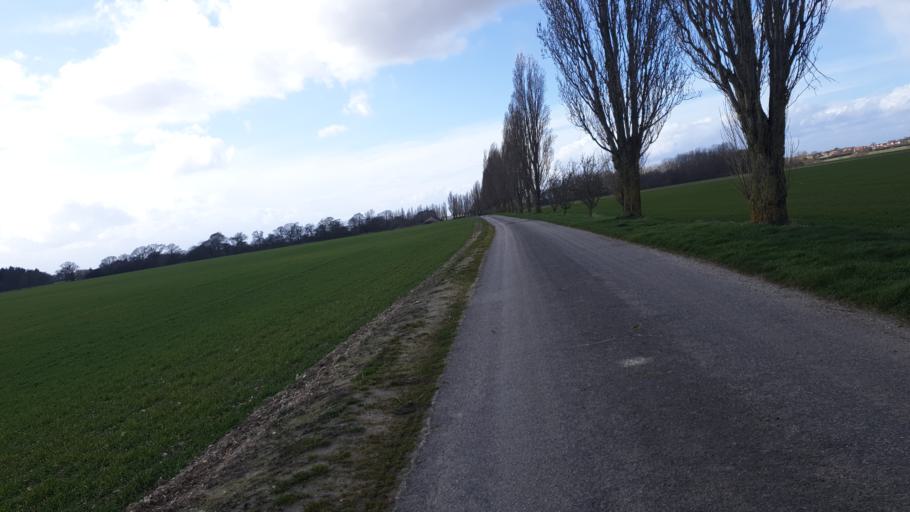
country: GB
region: England
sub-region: Essex
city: Little Clacton
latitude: 51.8499
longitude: 1.1382
